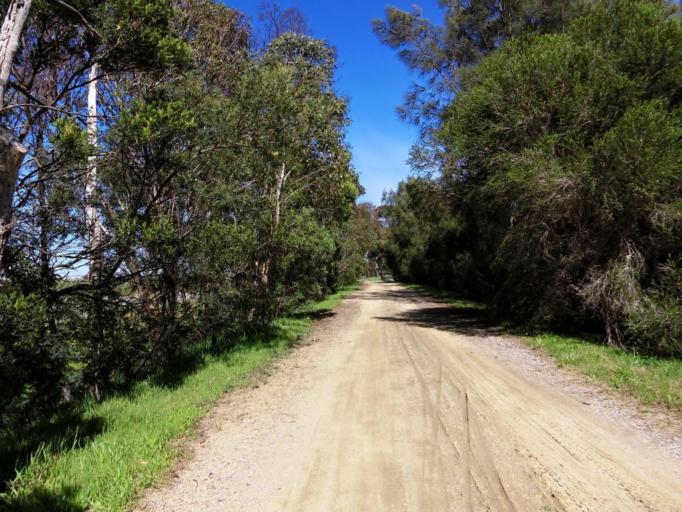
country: AU
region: Victoria
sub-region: Greater Dandenong
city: Keysborough
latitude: -38.0191
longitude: 145.1887
